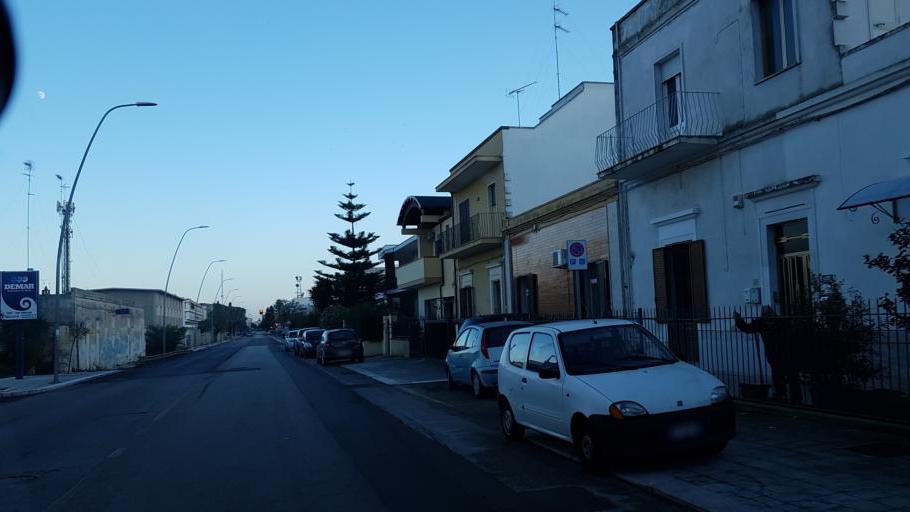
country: IT
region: Apulia
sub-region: Provincia di Lecce
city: Lecce
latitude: 40.3627
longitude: 18.1511
